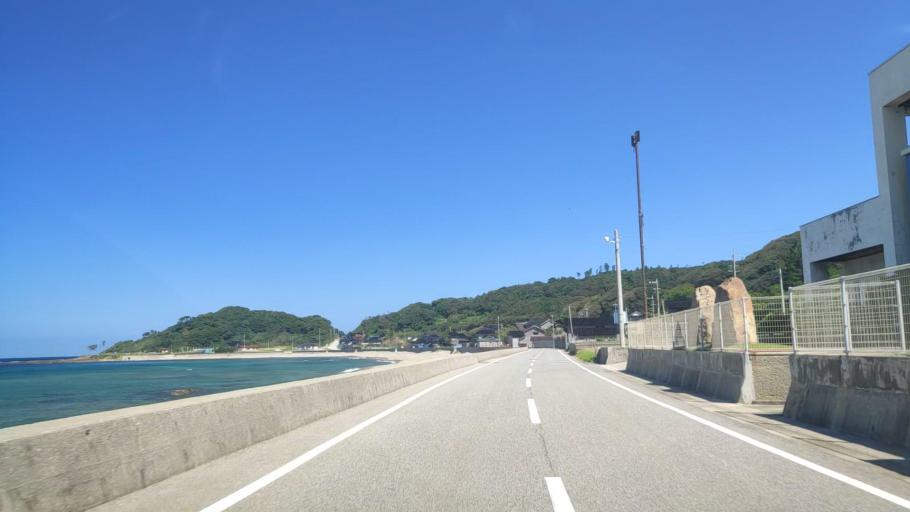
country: JP
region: Ishikawa
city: Nanao
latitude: 37.5084
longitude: 137.2163
